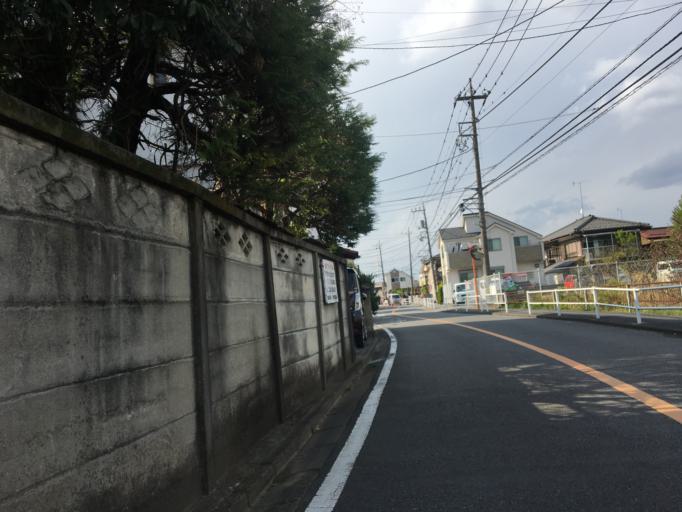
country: JP
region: Tokyo
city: Chofugaoka
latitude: 35.6454
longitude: 139.4939
